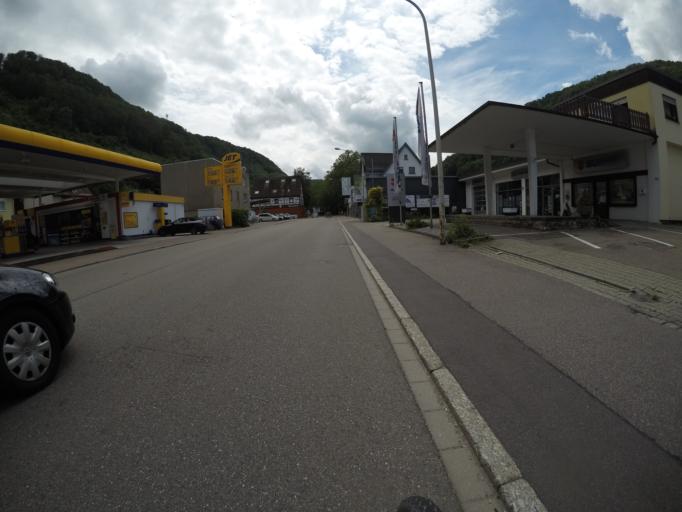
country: DE
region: Baden-Wuerttemberg
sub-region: Regierungsbezirk Stuttgart
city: Geislingen an der Steige
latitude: 48.6090
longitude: 9.8428
